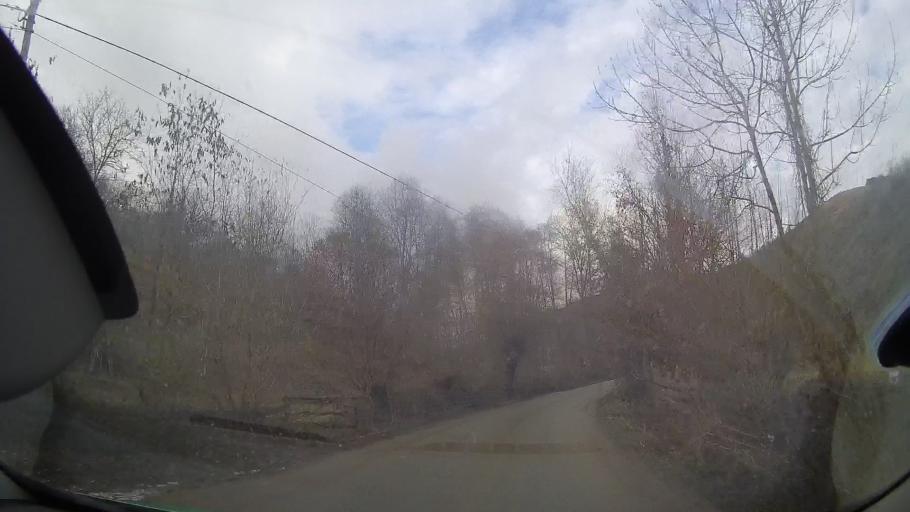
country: RO
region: Alba
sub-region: Comuna Ocolis
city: Ocolis
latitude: 46.4692
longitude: 23.4764
